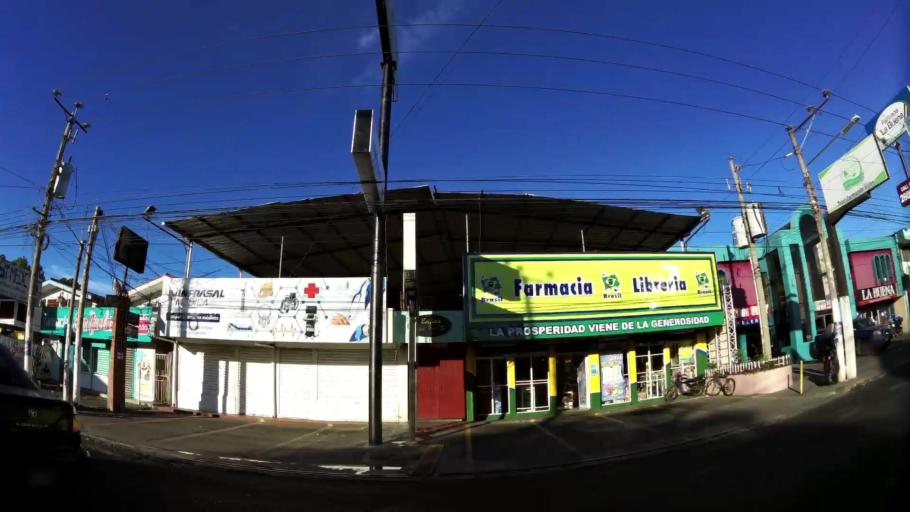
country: SV
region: San Miguel
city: San Miguel
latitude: 13.4775
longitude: -88.1844
